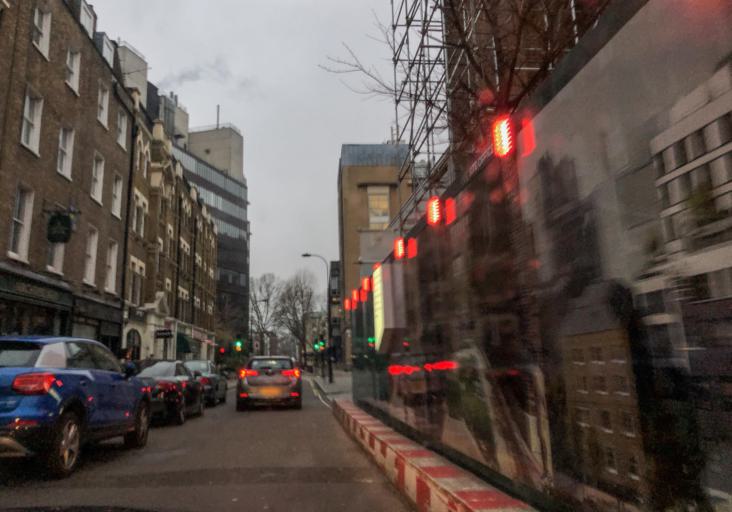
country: GB
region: England
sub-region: Greater London
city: London
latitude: 51.5204
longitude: -0.1385
